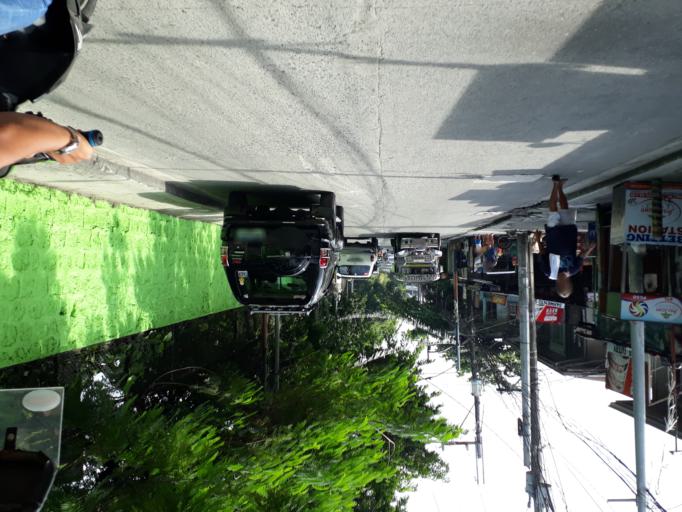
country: PH
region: Calabarzon
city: Bagong Pagasa
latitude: 14.6718
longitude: 121.0056
